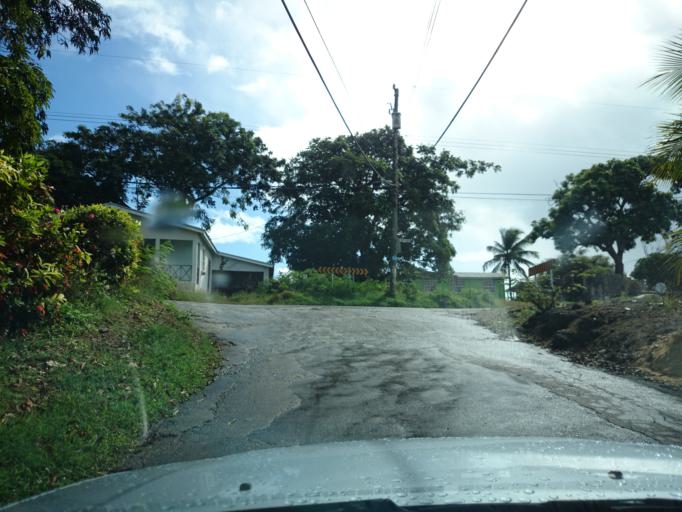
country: BB
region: Saint Peter
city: Speightstown
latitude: 13.2283
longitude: -59.6283
